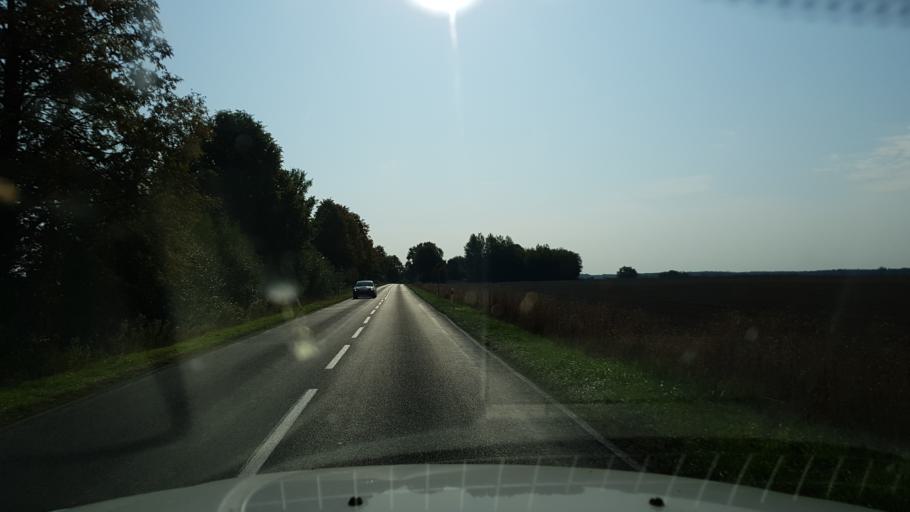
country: PL
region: West Pomeranian Voivodeship
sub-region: Powiat gryficki
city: Ploty
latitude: 53.7898
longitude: 15.3006
